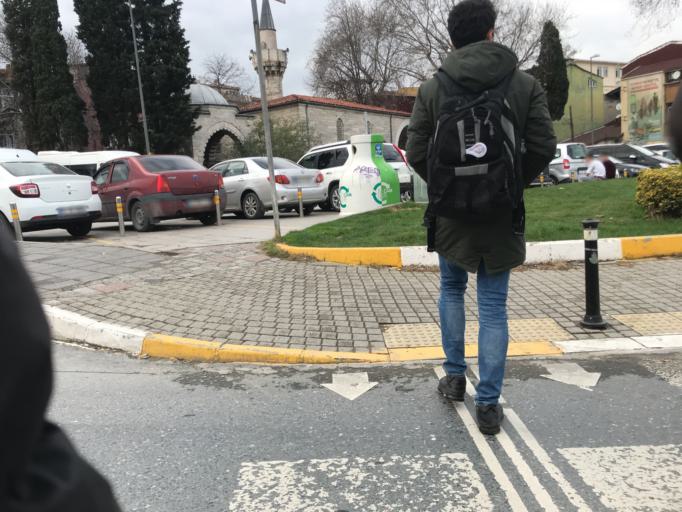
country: TR
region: Istanbul
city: Istanbul
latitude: 41.0419
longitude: 28.9382
